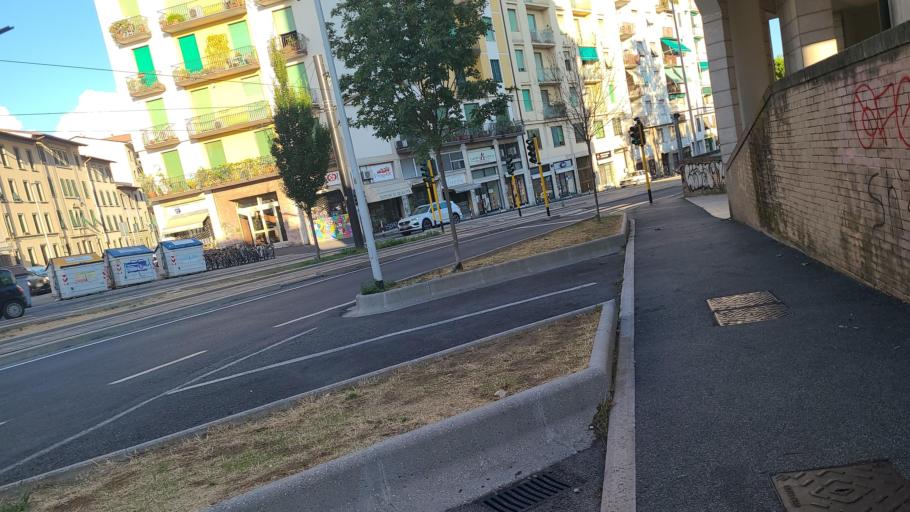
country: IT
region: Tuscany
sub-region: Province of Florence
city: Florence
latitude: 43.7927
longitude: 11.2460
